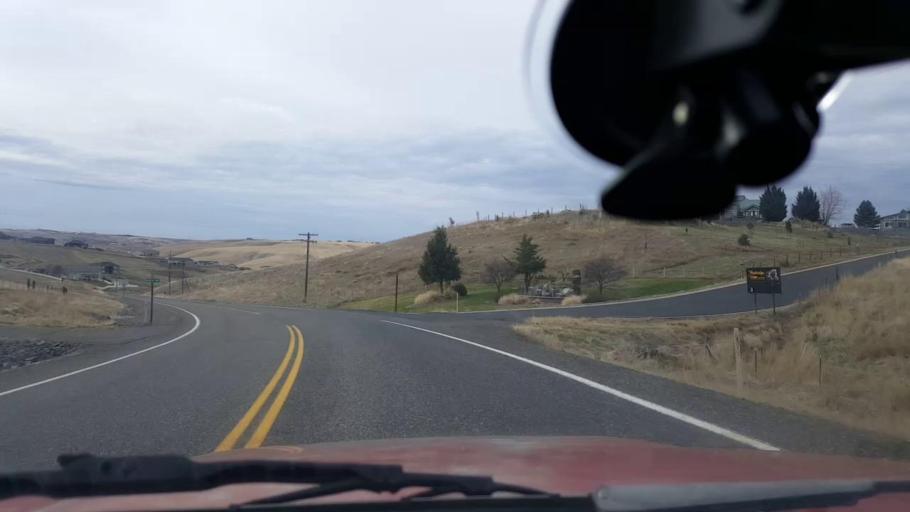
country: US
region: Washington
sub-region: Asotin County
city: Clarkston Heights-Vineland
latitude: 46.4021
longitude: -117.0881
